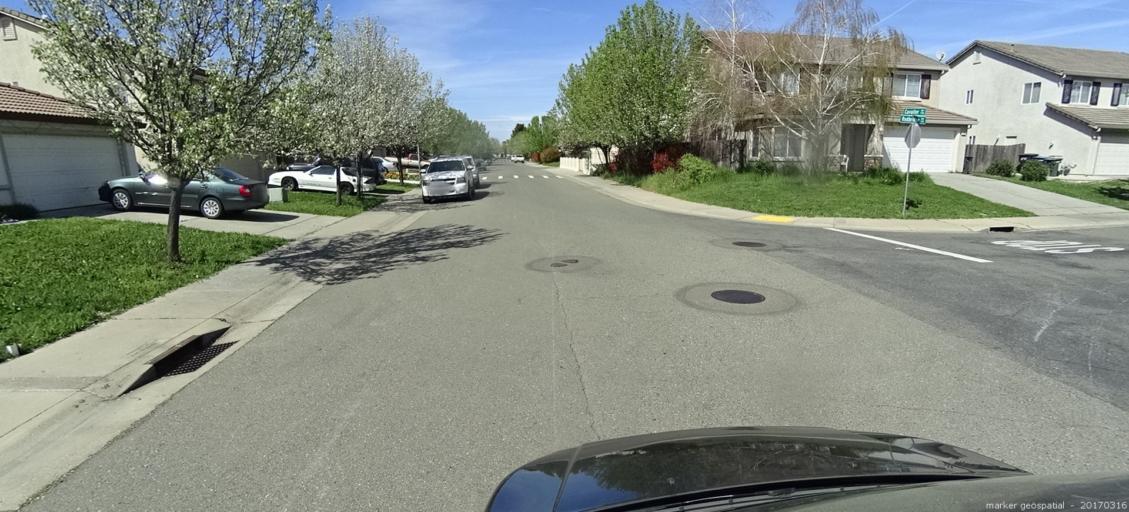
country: US
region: California
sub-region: Sacramento County
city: Parkway
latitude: 38.4713
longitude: -121.4984
